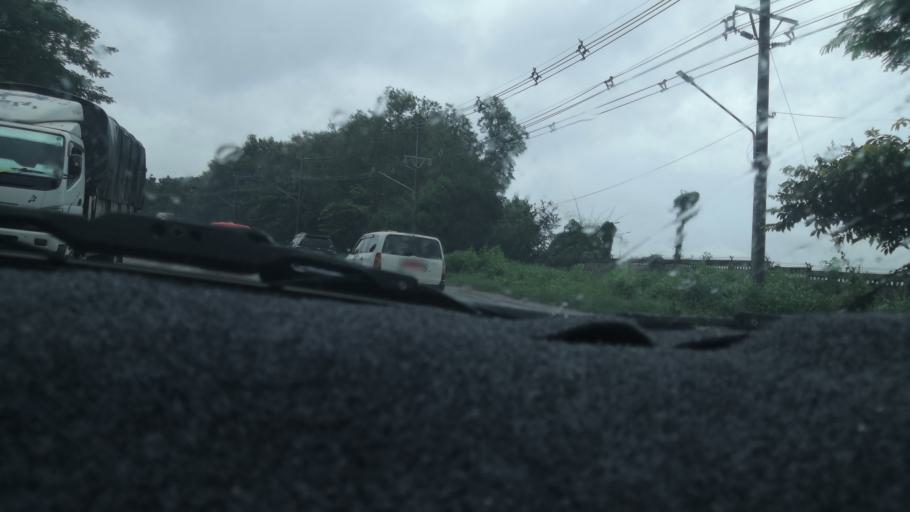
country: MM
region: Yangon
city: Yangon
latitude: 16.9133
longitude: 96.1342
